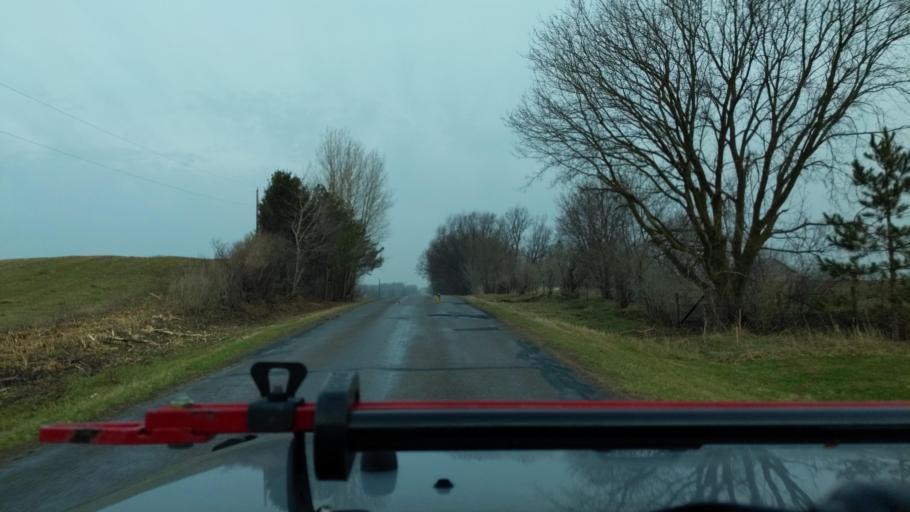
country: US
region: Wisconsin
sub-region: Saint Croix County
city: Baldwin
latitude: 44.9346
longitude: -92.3795
